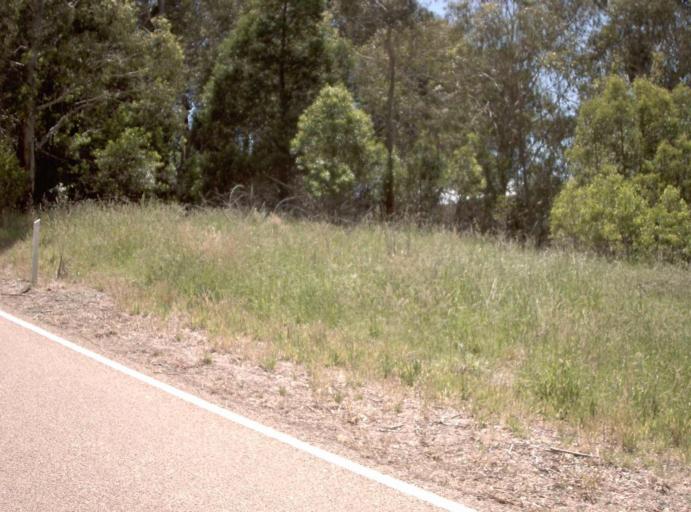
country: AU
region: Victoria
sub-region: East Gippsland
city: Lakes Entrance
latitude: -37.2152
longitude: 148.2680
